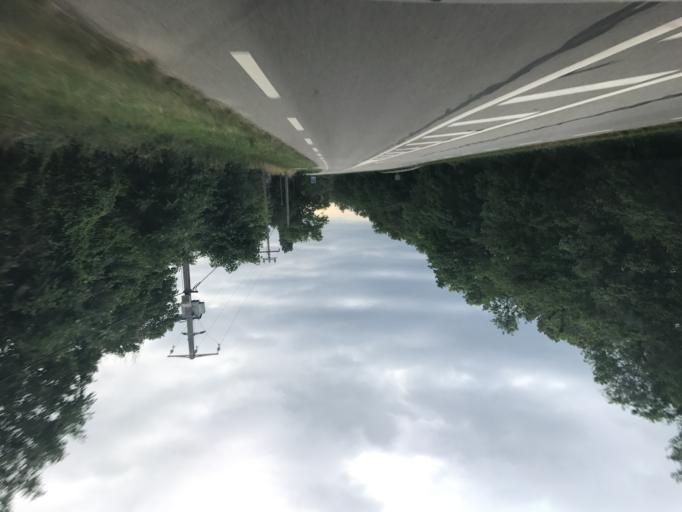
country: FR
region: Rhone-Alpes
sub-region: Departement de l'Ardeche
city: Charmes-sur-Rhone
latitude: 44.8560
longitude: 4.8523
